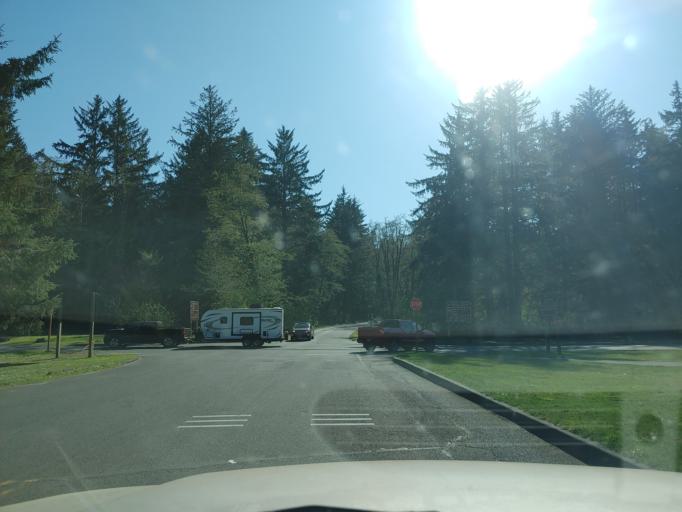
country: US
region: Oregon
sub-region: Clatsop County
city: Warrenton
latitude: 46.1817
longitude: -123.9625
